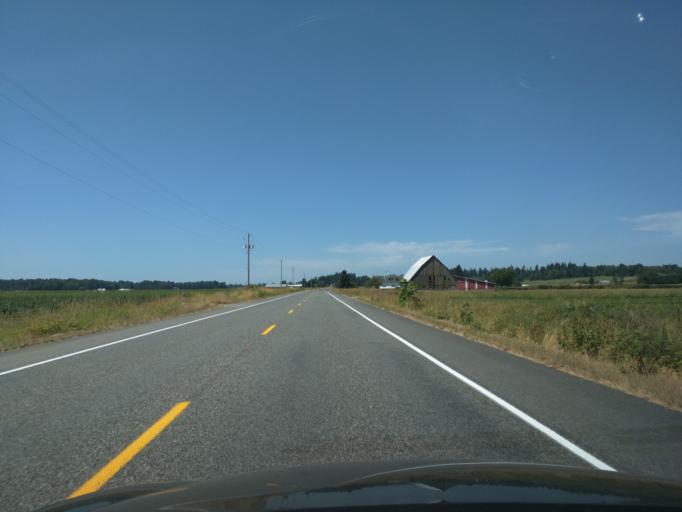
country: US
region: Washington
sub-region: Whatcom County
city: Lynden
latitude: 48.9648
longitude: -122.5372
